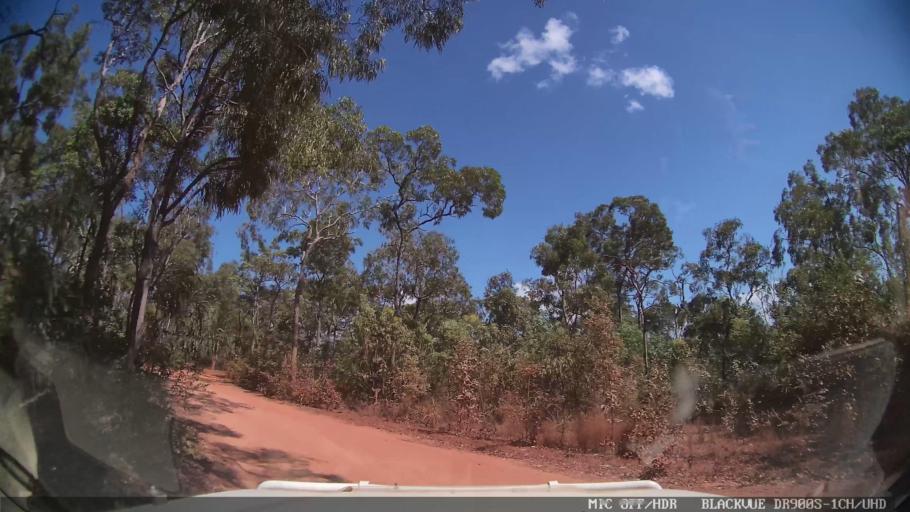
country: AU
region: Queensland
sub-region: Torres
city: Thursday Island
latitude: -11.4421
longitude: 142.4306
